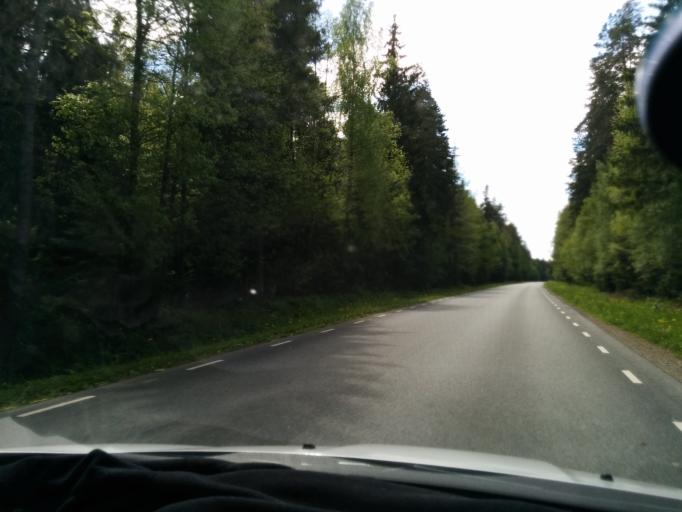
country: EE
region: Harju
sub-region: Loksa linn
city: Loksa
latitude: 59.5448
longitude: 25.7626
